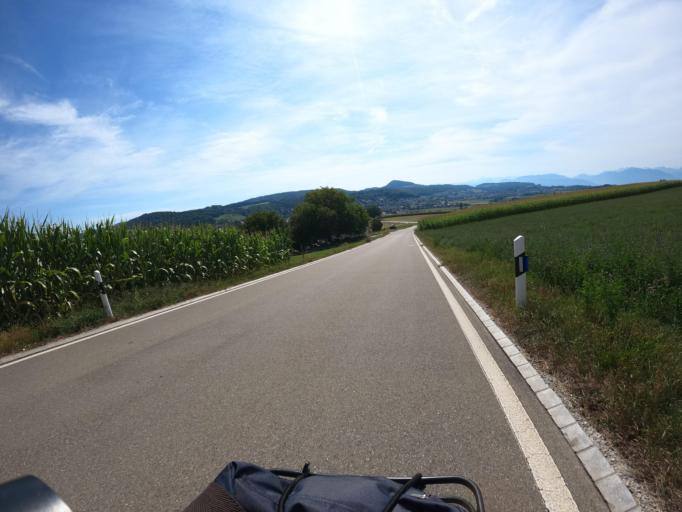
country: CH
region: Zurich
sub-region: Bezirk Affoltern
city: Hedingen
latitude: 47.3046
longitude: 8.4319
